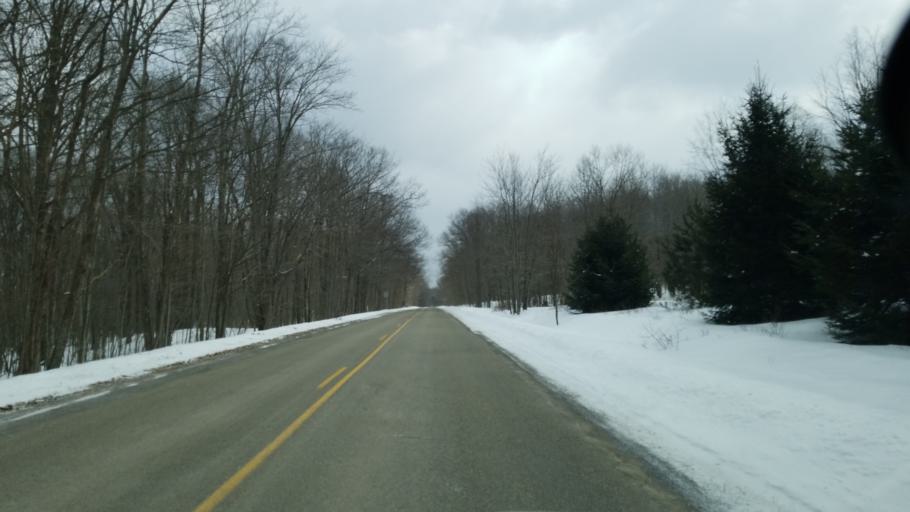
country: US
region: Pennsylvania
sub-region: Clearfield County
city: Shiloh
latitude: 41.2523
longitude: -78.3366
